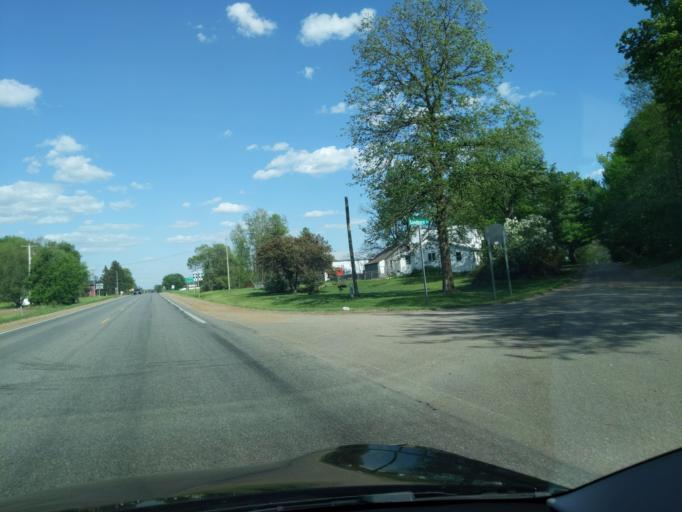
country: US
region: Michigan
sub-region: Ionia County
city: Lake Odessa
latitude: 42.7559
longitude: -85.0519
